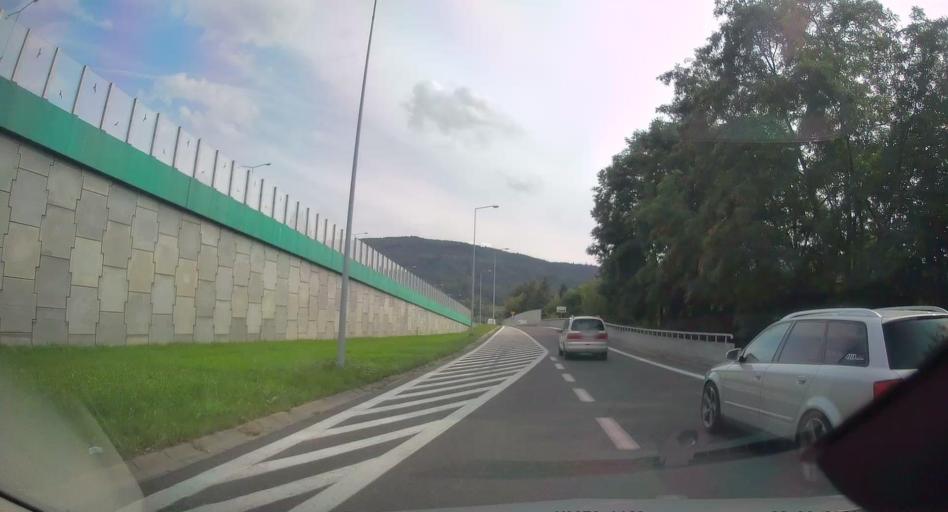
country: PL
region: Lesser Poland Voivodeship
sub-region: Powiat myslenicki
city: Myslenice
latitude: 49.8329
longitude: 19.9502
